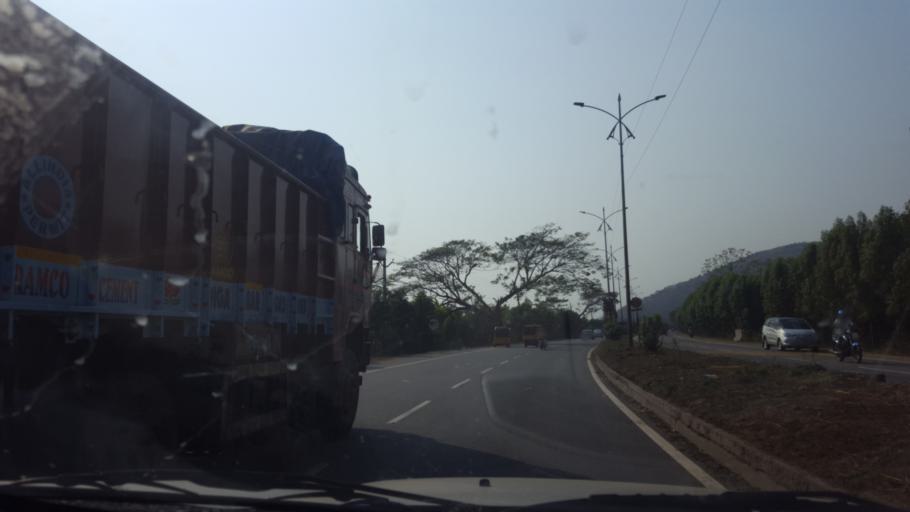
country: IN
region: Andhra Pradesh
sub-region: Vishakhapatnam
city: Anakapalle
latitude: 17.6862
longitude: 83.0816
